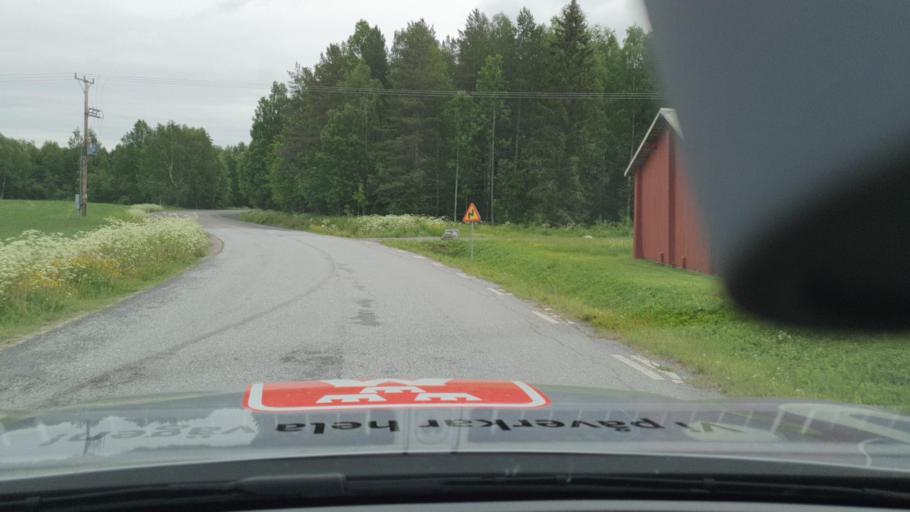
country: SE
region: Norrbotten
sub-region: Lulea Kommun
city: Ranea
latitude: 65.8481
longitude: 22.2872
